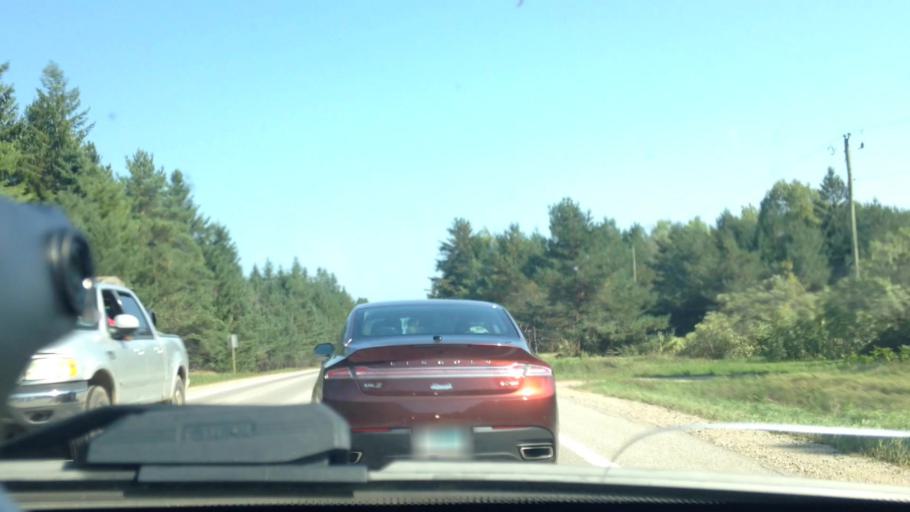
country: US
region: Michigan
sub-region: Luce County
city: Newberry
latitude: 46.3037
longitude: -85.4451
